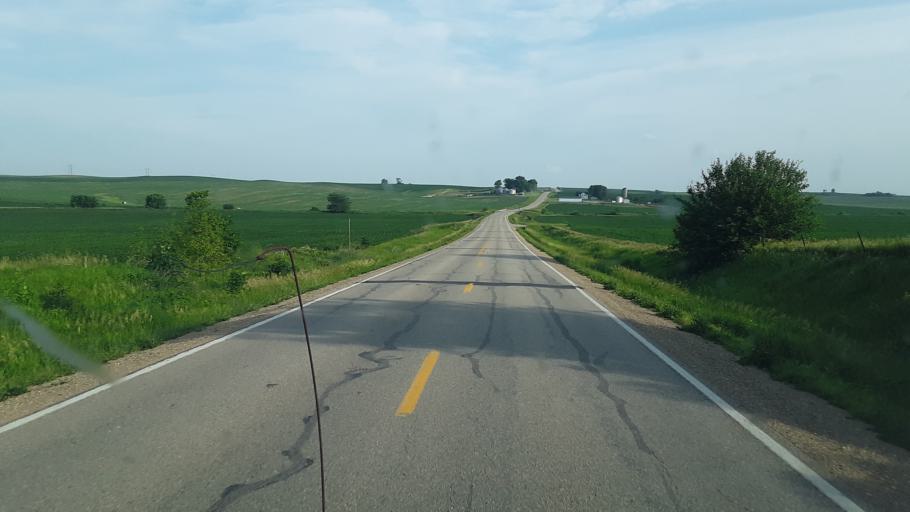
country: US
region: Iowa
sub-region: Tama County
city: Tama
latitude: 41.9527
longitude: -92.7078
